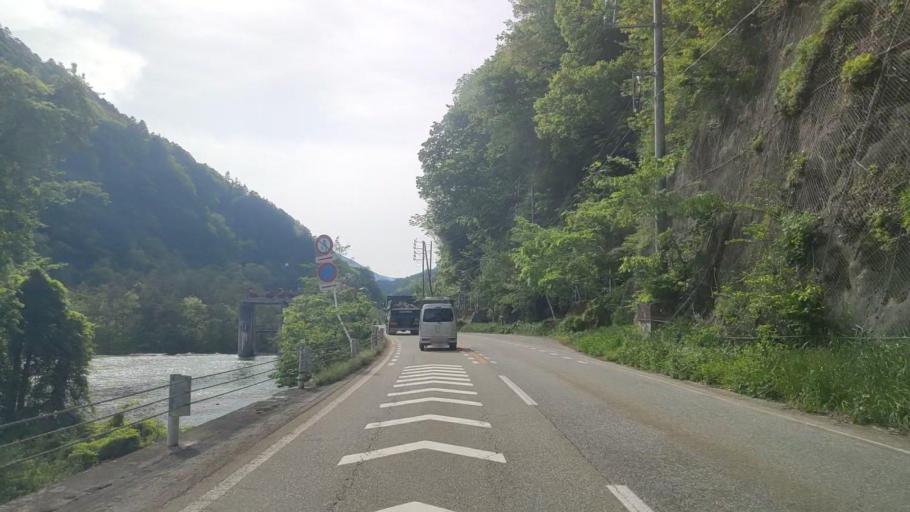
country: JP
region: Gifu
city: Takayama
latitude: 36.2653
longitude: 137.4285
